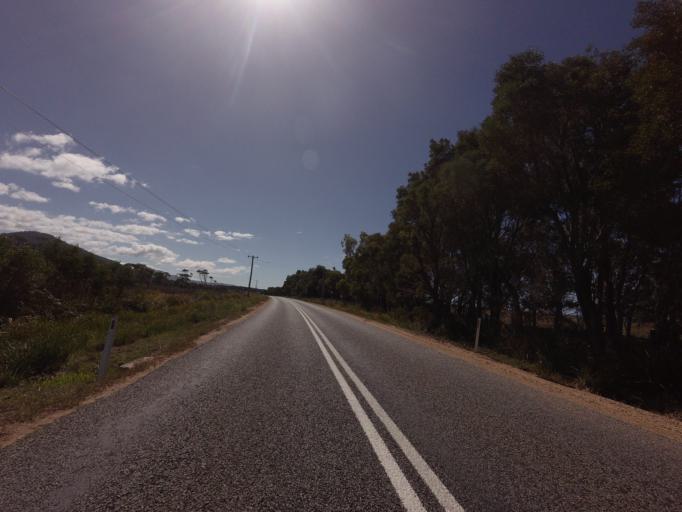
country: AU
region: Tasmania
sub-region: Break O'Day
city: St Helens
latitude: -41.7686
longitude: 148.2709
